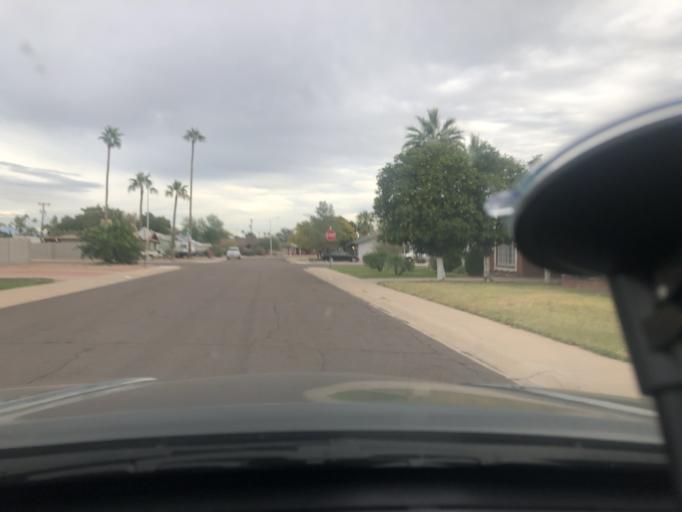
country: US
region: Arizona
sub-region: Maricopa County
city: Scottsdale
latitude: 33.4833
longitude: -111.9009
